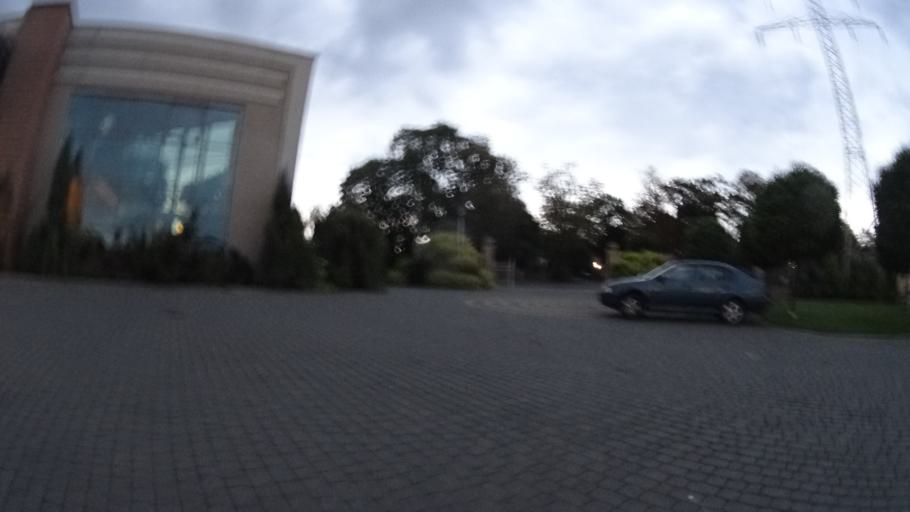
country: PL
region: Masovian Voivodeship
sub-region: Powiat warszawski zachodni
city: Babice
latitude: 52.2281
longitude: 20.8594
